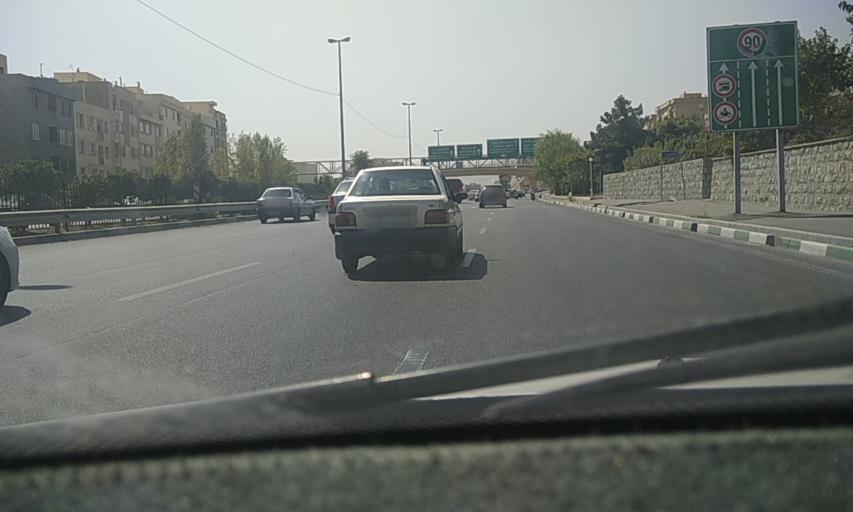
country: IR
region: Tehran
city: Tajrish
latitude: 35.7701
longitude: 51.3259
